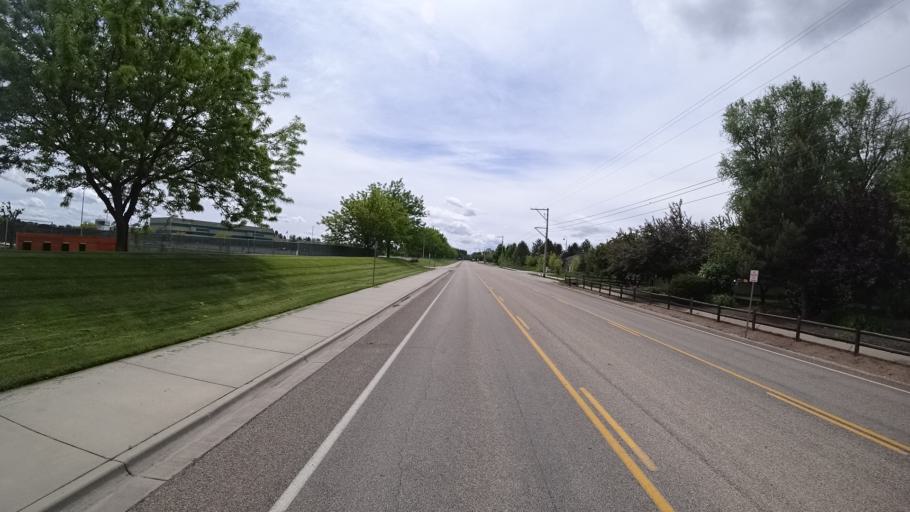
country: US
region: Idaho
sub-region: Ada County
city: Eagle
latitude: 43.7031
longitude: -116.4036
